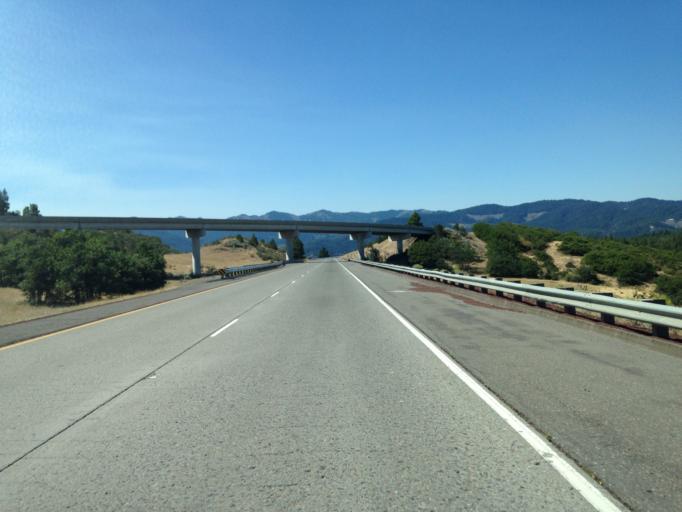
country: US
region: Oregon
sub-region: Jackson County
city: Ashland
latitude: 42.0198
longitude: -122.6101
